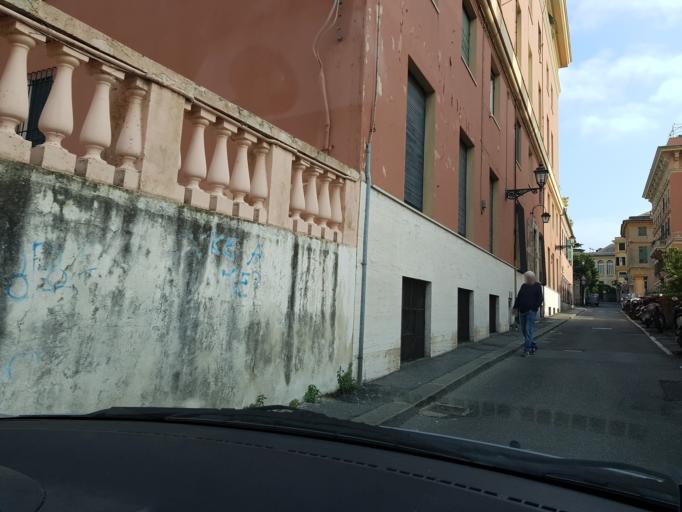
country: IT
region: Liguria
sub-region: Provincia di Genova
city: San Teodoro
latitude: 44.3996
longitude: 8.9583
